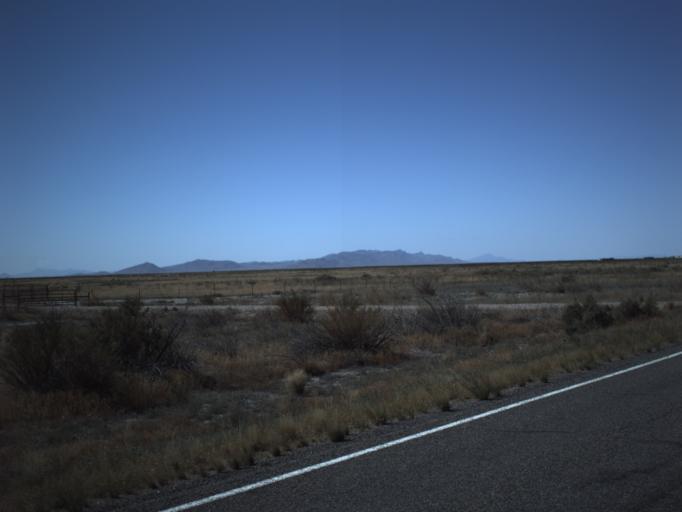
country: US
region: Utah
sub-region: Millard County
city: Delta
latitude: 39.2932
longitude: -112.8237
